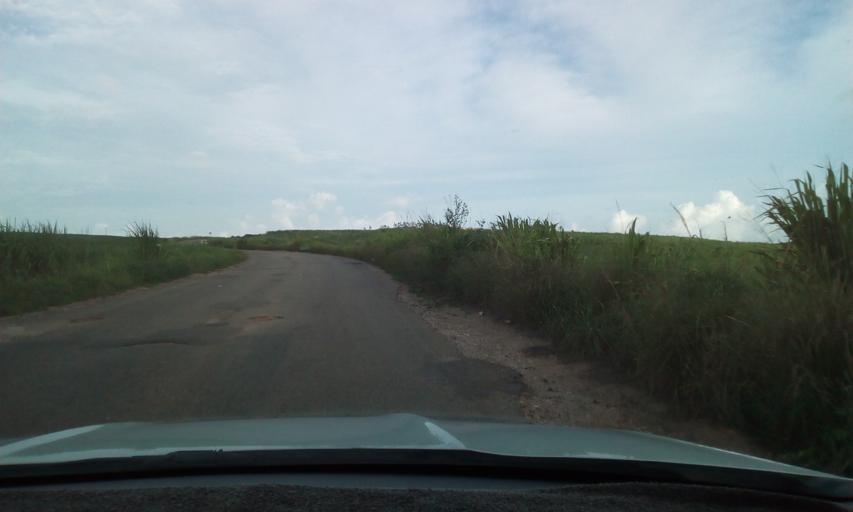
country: BR
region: Pernambuco
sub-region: Gloria Do Goita
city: Gloria do Goita
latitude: -7.9901
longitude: -35.2332
